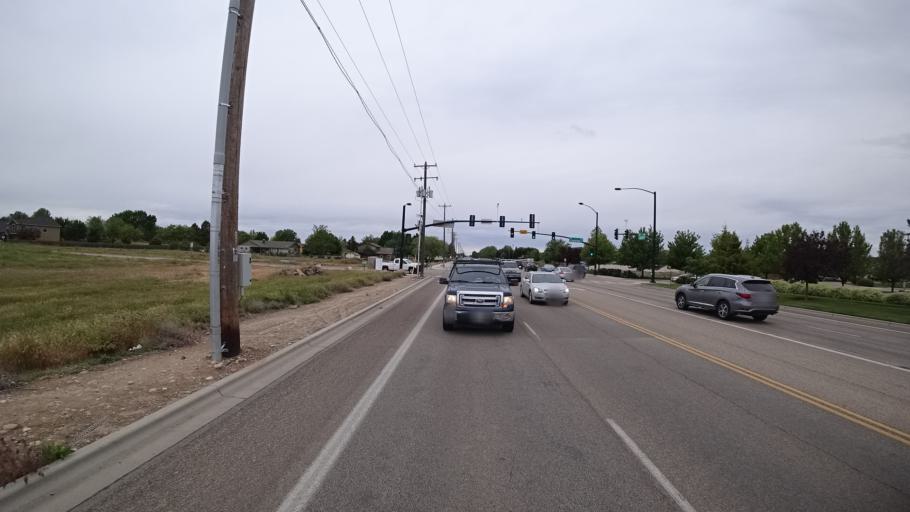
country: US
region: Idaho
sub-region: Ada County
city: Meridian
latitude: 43.6338
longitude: -116.3583
